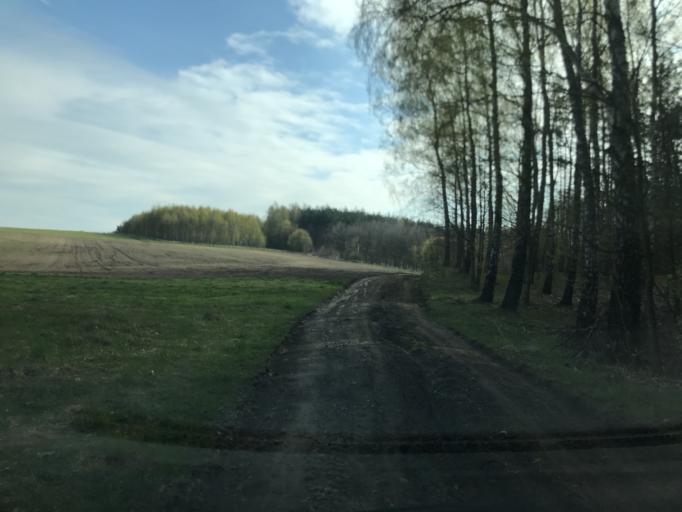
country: PL
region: Warmian-Masurian Voivodeship
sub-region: Powiat ostrodzki
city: Dabrowno
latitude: 53.3877
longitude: 20.0086
